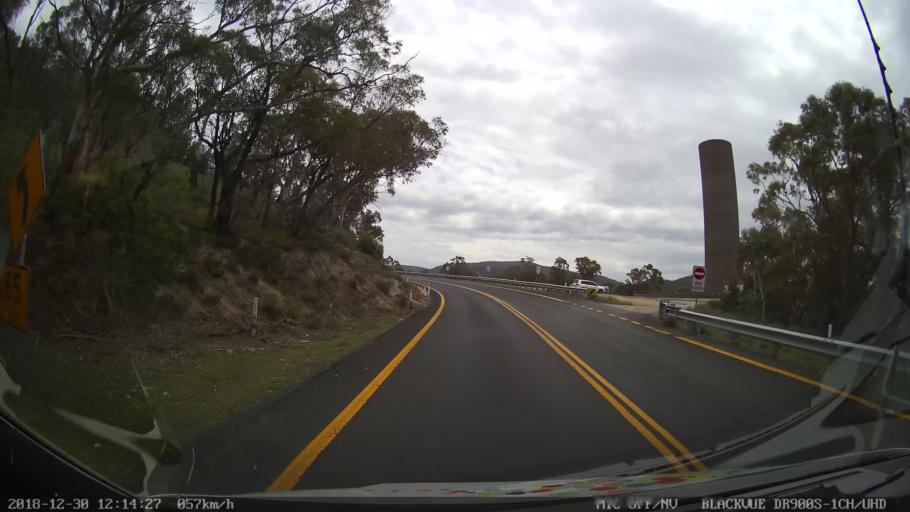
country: AU
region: New South Wales
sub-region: Snowy River
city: Jindabyne
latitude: -36.3431
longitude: 148.5805
